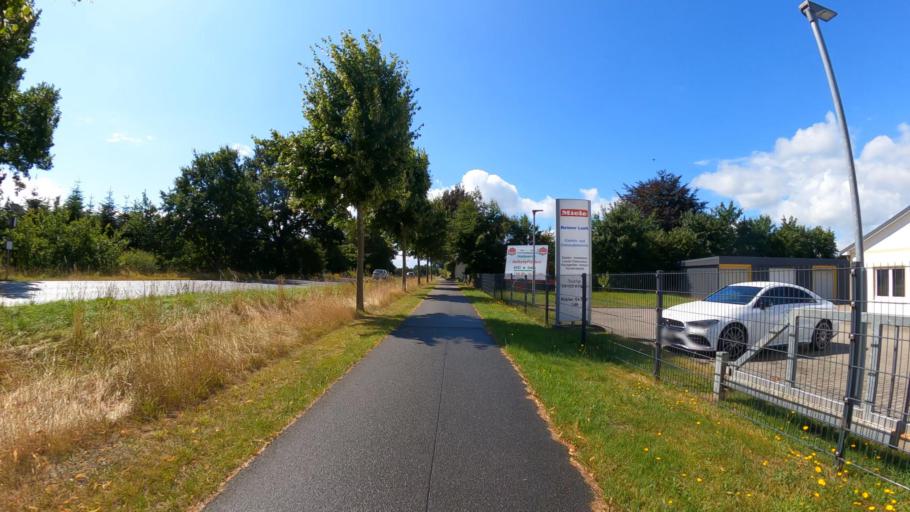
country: DE
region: Schleswig-Holstein
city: Wiemersdorf
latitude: 53.9479
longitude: 9.8985
